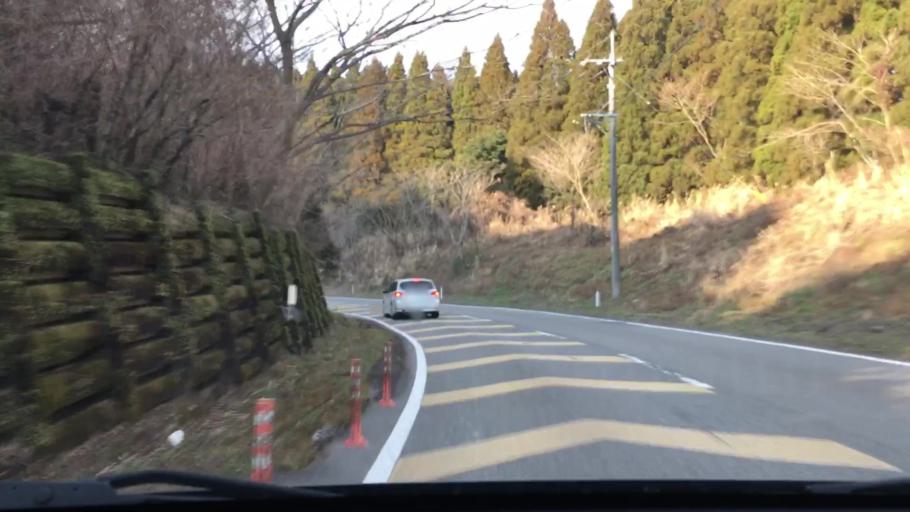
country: JP
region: Miyazaki
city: Miyazaki-shi
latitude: 31.7891
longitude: 131.3201
